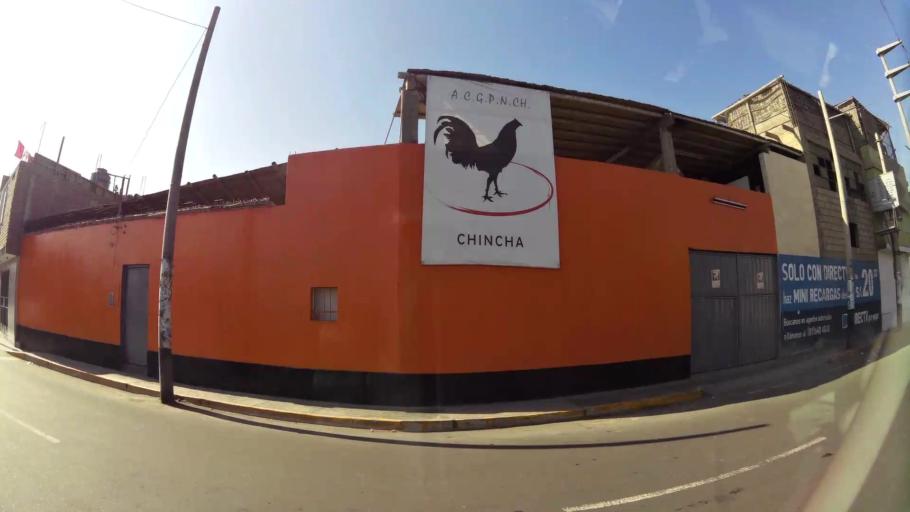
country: PE
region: Ica
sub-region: Provincia de Chincha
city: Chincha Alta
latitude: -13.4209
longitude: -76.1343
